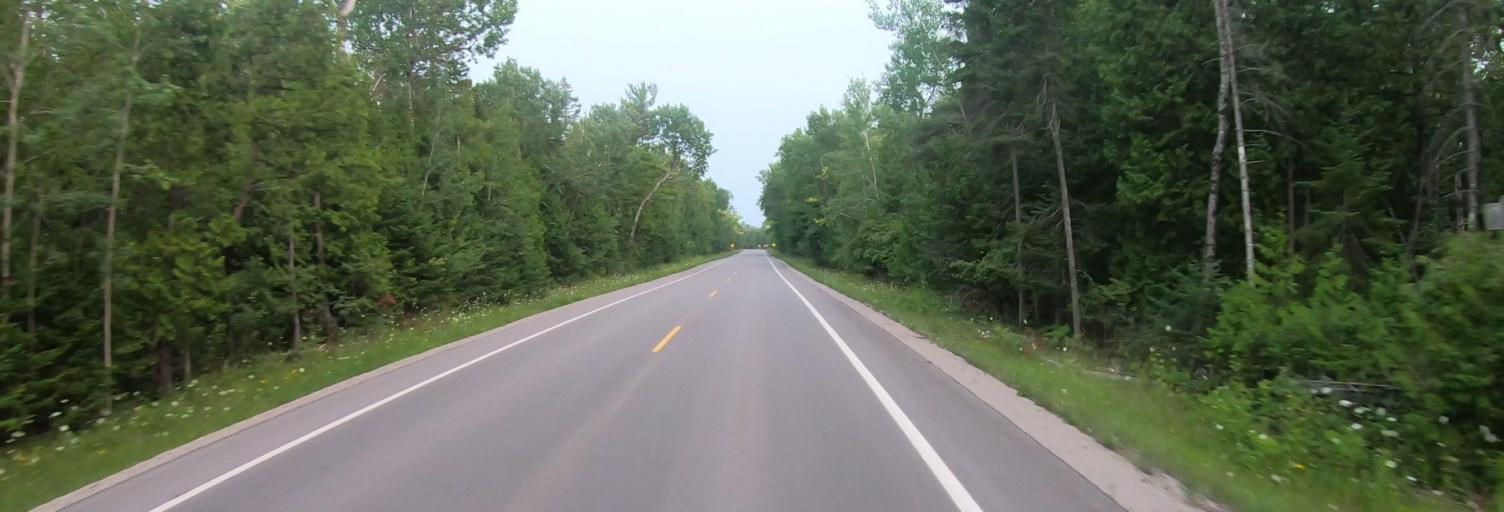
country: US
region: Michigan
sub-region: Mackinac County
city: Saint Ignace
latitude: 45.7711
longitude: -84.7731
